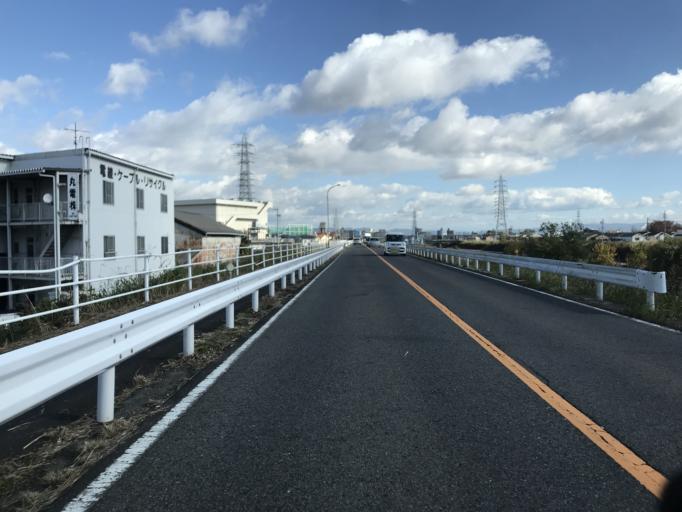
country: JP
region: Aichi
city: Nagoya-shi
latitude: 35.2324
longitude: 136.8928
